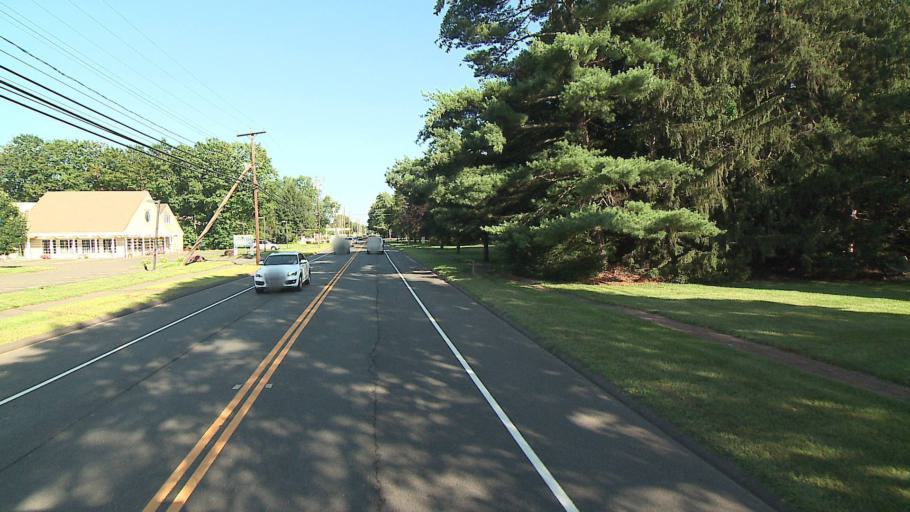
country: US
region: Connecticut
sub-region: Hartford County
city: Farmington
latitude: 41.7353
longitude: -72.8385
